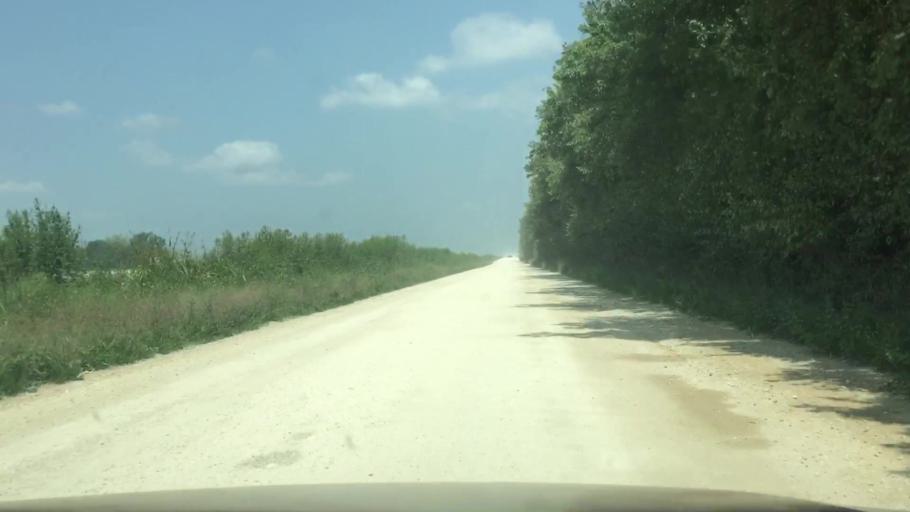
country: US
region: Kansas
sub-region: Allen County
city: Humboldt
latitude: 37.8290
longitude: -95.4093
